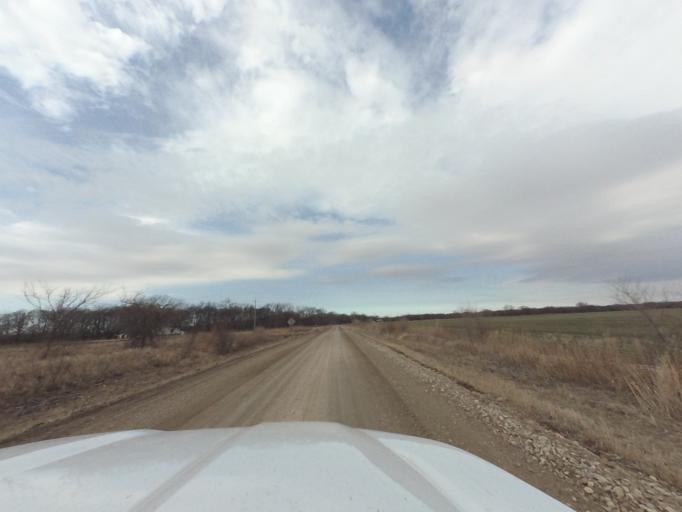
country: US
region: Kansas
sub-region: Chase County
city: Cottonwood Falls
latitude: 38.2973
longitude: -96.7340
